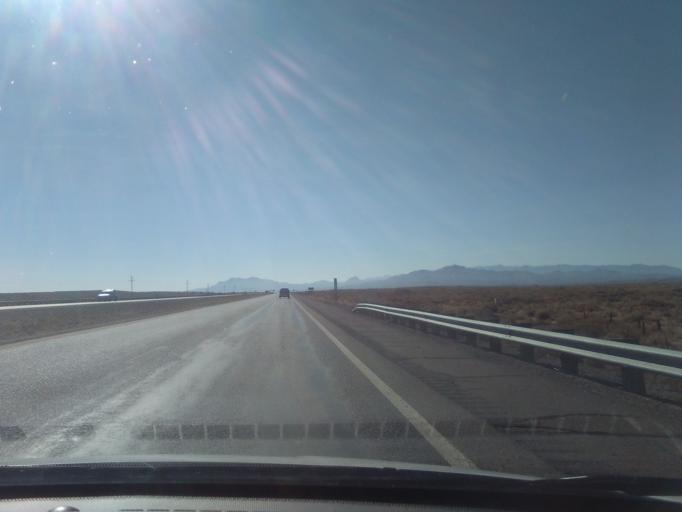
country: US
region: New Mexico
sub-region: Socorro County
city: Socorro
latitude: 34.3237
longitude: -106.8826
